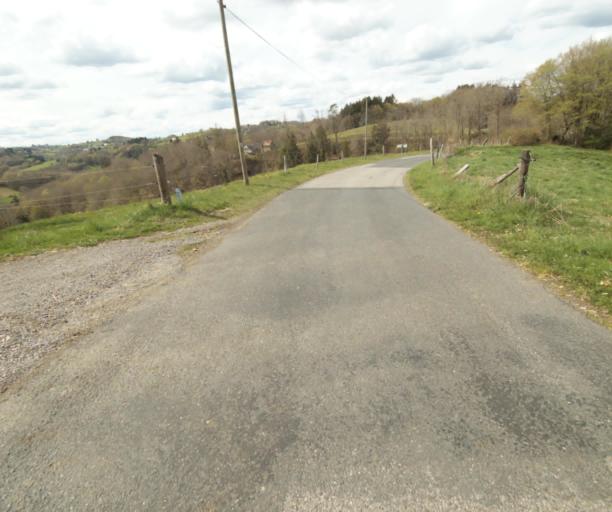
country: FR
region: Limousin
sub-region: Departement de la Correze
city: Laguenne
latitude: 45.2371
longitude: 1.8578
